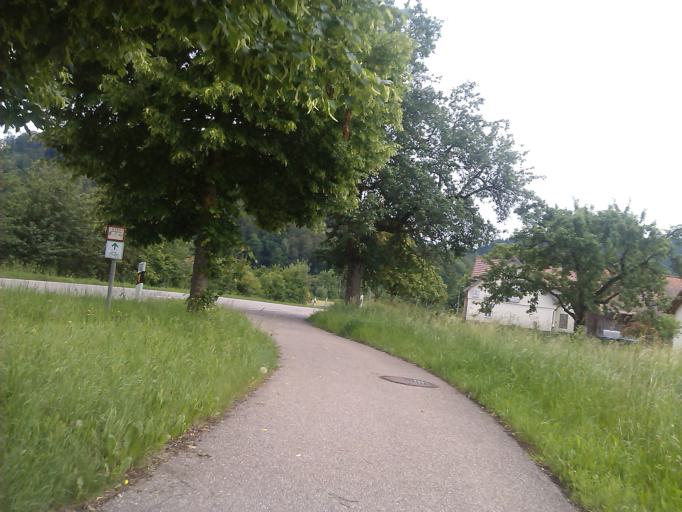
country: DE
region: Baden-Wuerttemberg
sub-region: Regierungsbezirk Stuttgart
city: Gaildorf
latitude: 48.9750
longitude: 9.7888
